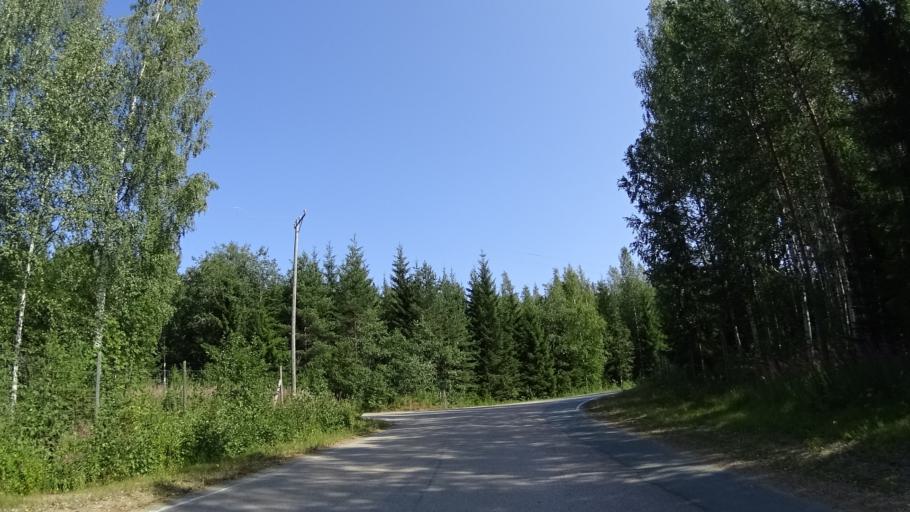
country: FI
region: Central Finland
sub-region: Jaemsae
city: Jaemsae
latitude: 61.7750
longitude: 24.8927
